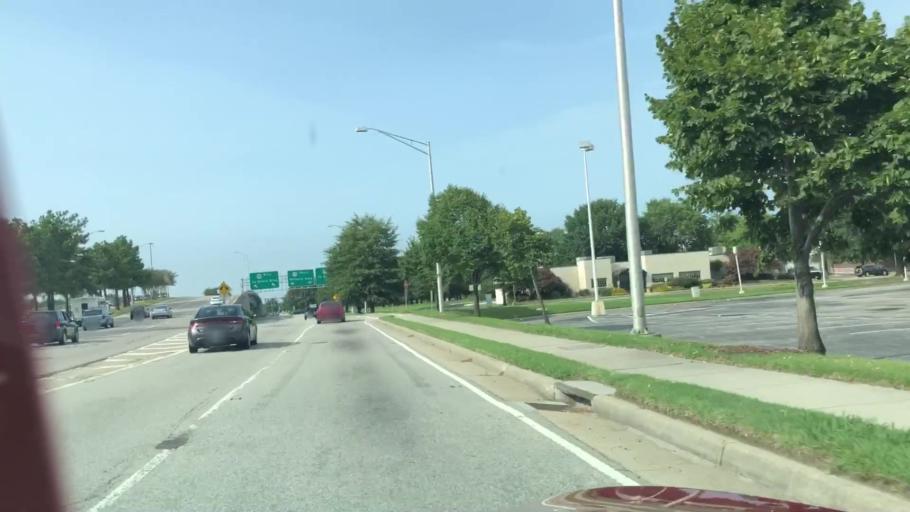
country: US
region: Virginia
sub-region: City of Chesapeake
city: Chesapeake
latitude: 36.8533
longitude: -76.2097
